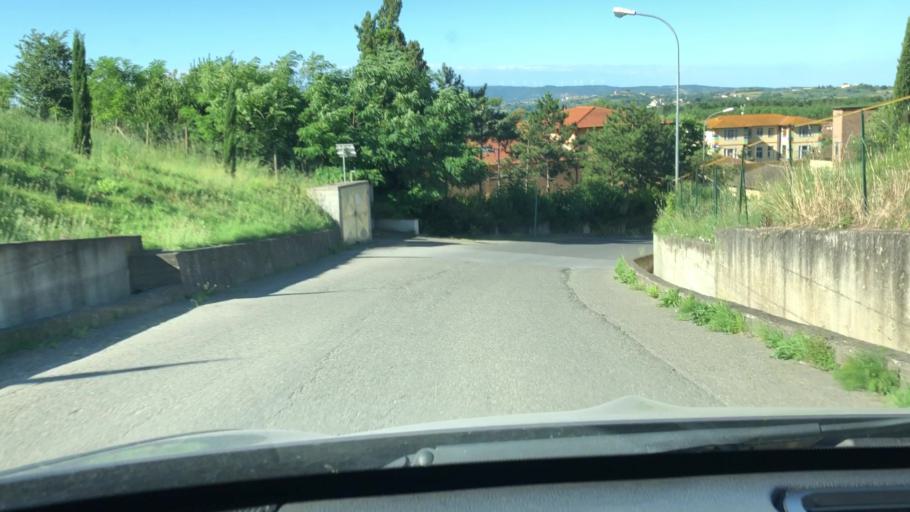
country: IT
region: Tuscany
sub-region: Province of Pisa
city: Forcoli
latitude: 43.6053
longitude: 10.7051
